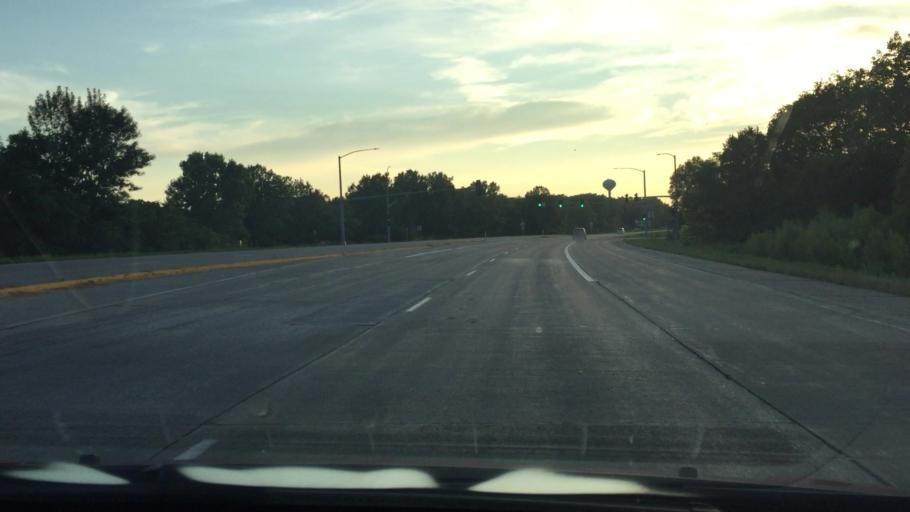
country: US
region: Iowa
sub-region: Muscatine County
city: Muscatine
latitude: 41.4519
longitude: -91.0407
